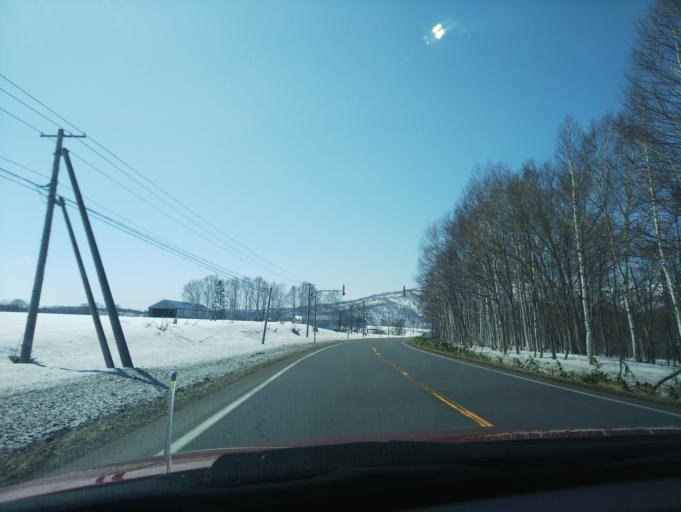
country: JP
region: Hokkaido
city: Nayoro
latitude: 44.6581
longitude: 142.2721
